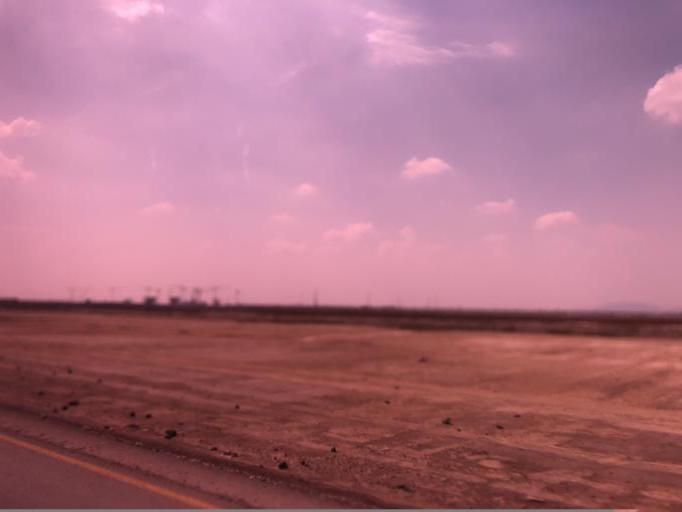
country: MX
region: Mexico
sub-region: Texcoco
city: Colonia Lazaro Cardenas
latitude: 19.5179
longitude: -98.9859
